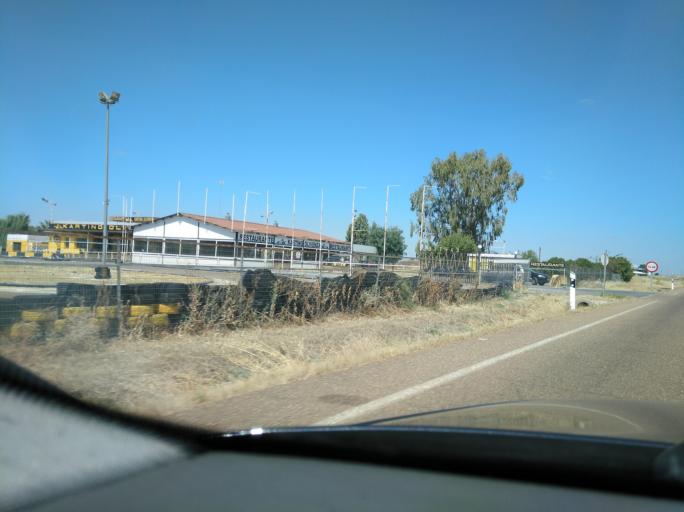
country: ES
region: Extremadura
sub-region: Provincia de Badajoz
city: Olivenza
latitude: 38.7033
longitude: -7.1091
